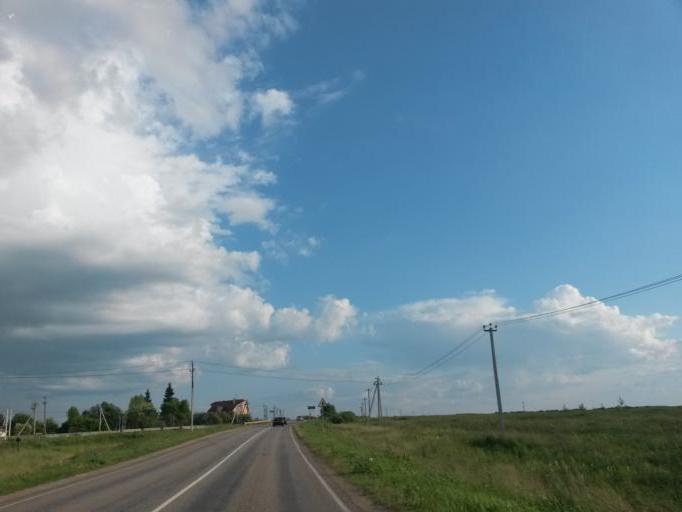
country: RU
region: Moskovskaya
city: Barybino
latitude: 55.2307
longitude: 37.7972
